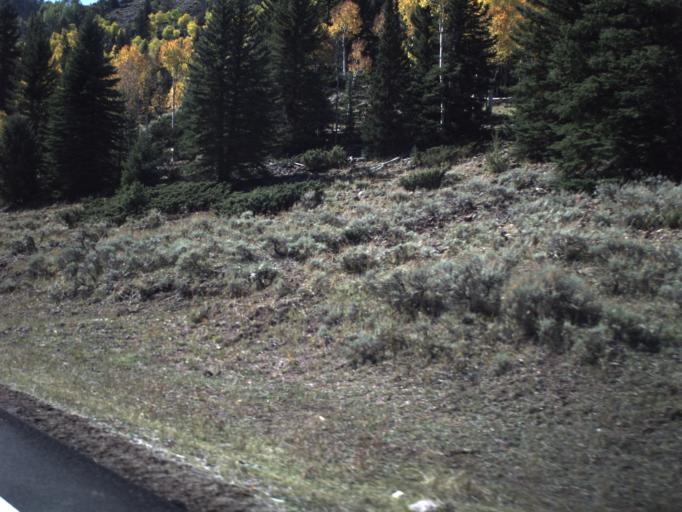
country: US
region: Utah
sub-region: Beaver County
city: Beaver
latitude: 38.2934
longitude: -112.4411
